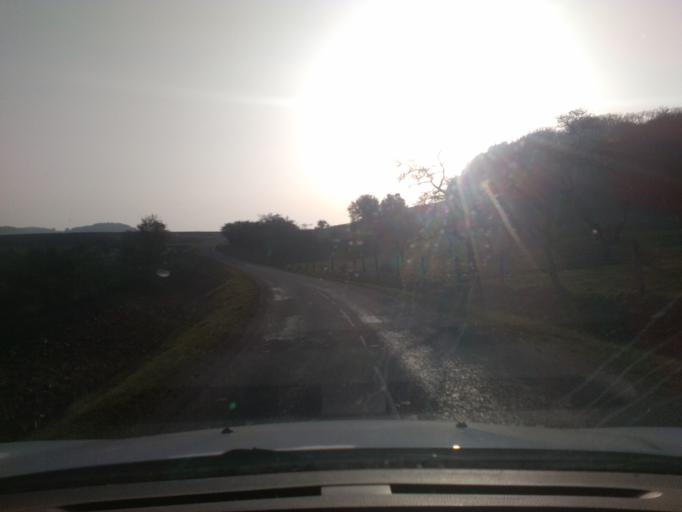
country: FR
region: Lorraine
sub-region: Departement des Vosges
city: Vittel
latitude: 48.2676
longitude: 6.0127
